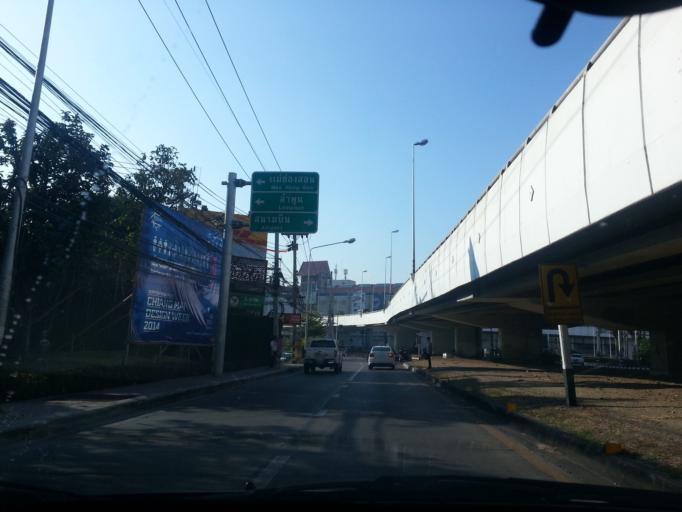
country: TH
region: Chiang Mai
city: Chiang Mai
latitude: 18.7713
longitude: 98.9761
